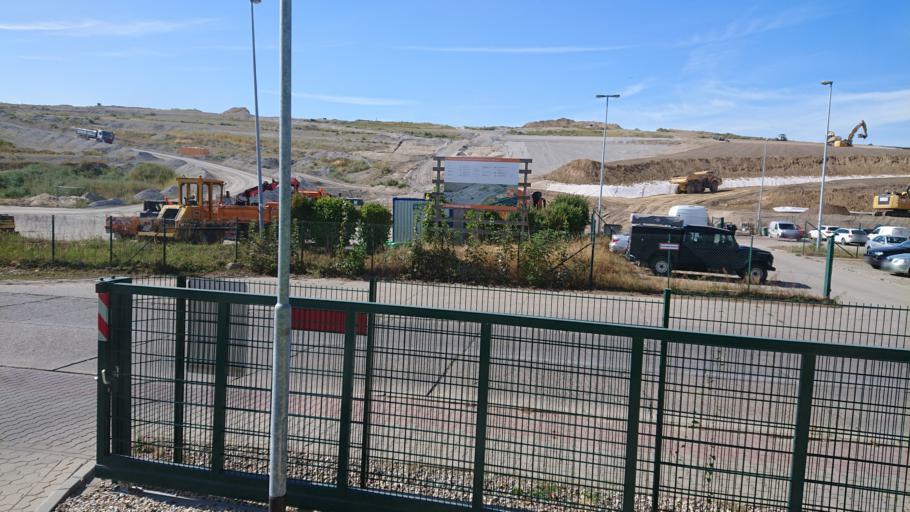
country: DE
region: Berlin
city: Buch
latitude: 52.6390
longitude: 13.5462
